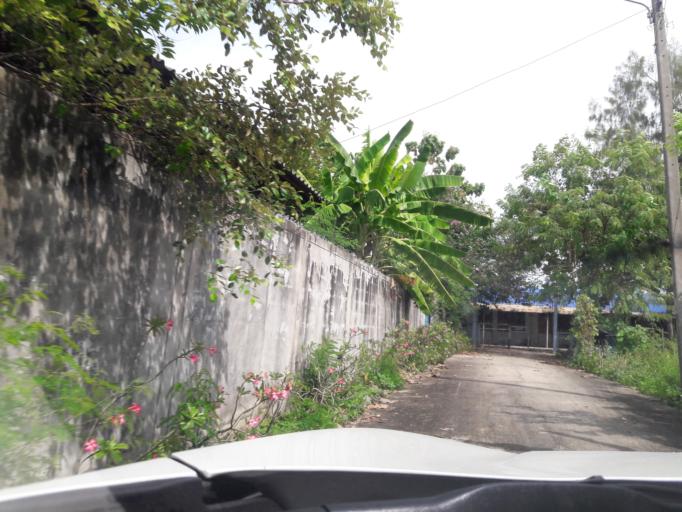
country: TH
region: Lop Buri
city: Ban Mi
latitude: 15.0433
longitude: 100.5522
